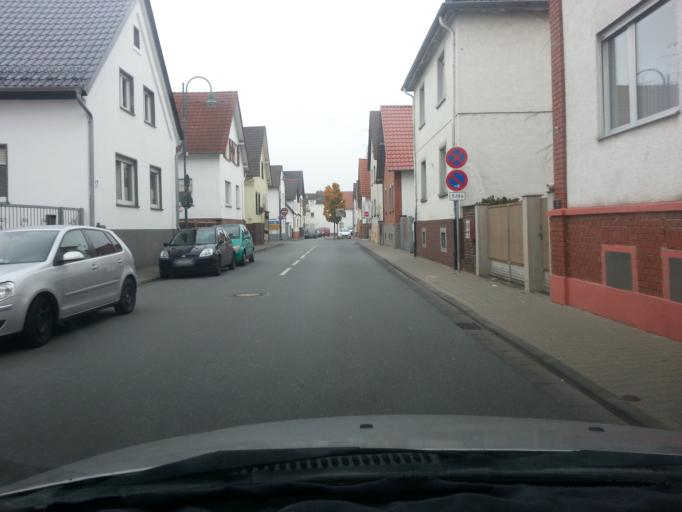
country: DE
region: Hesse
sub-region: Regierungsbezirk Darmstadt
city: Erzhausen
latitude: 49.9526
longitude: 8.6358
